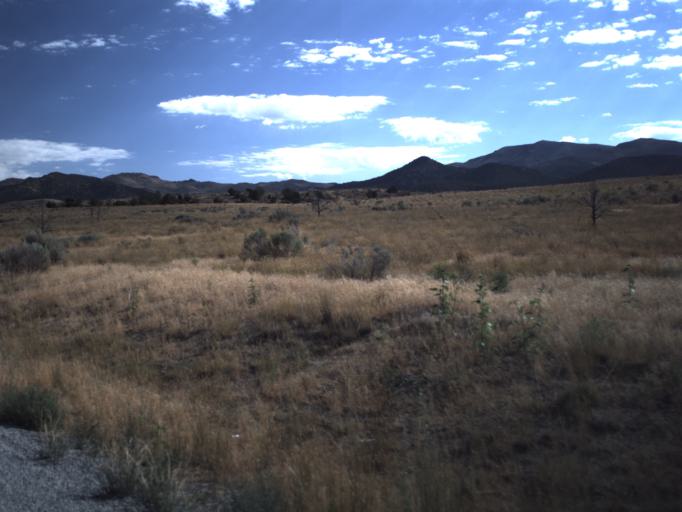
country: US
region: Utah
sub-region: Juab County
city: Mona
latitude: 39.7923
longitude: -112.1481
